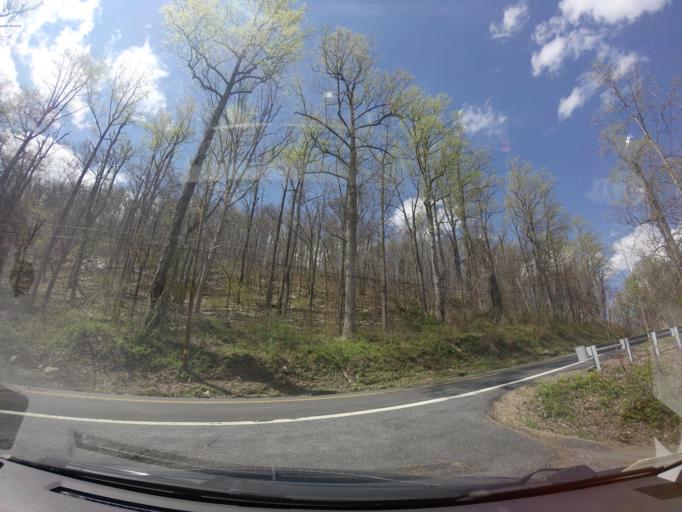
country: US
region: Maryland
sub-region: Frederick County
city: Brunswick
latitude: 39.4021
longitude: -77.6375
